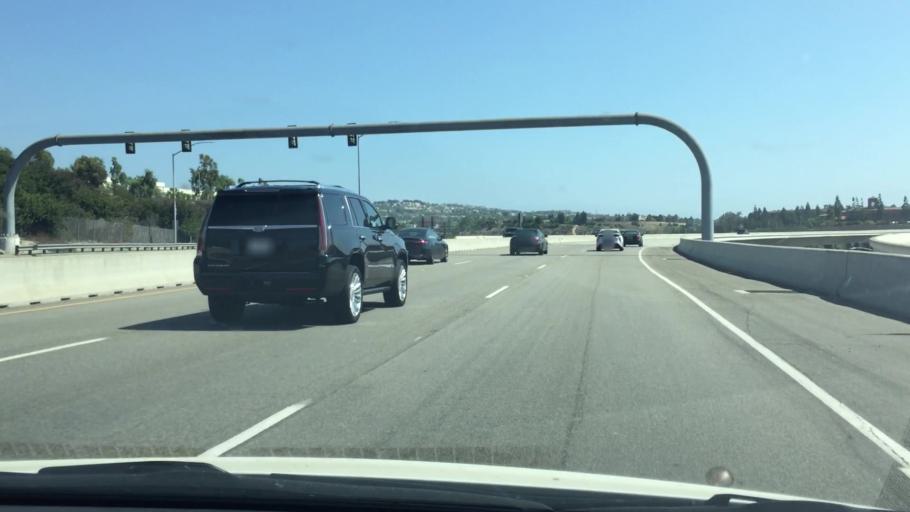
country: US
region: California
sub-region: Orange County
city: San Joaquin Hills
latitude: 33.6448
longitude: -117.8596
